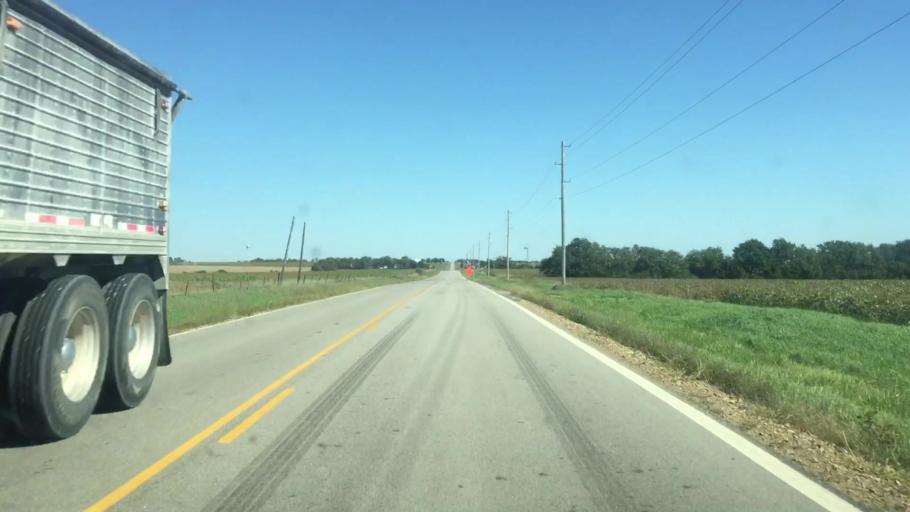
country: US
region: Kansas
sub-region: Jackson County
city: Holton
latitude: 39.5950
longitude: -95.6841
